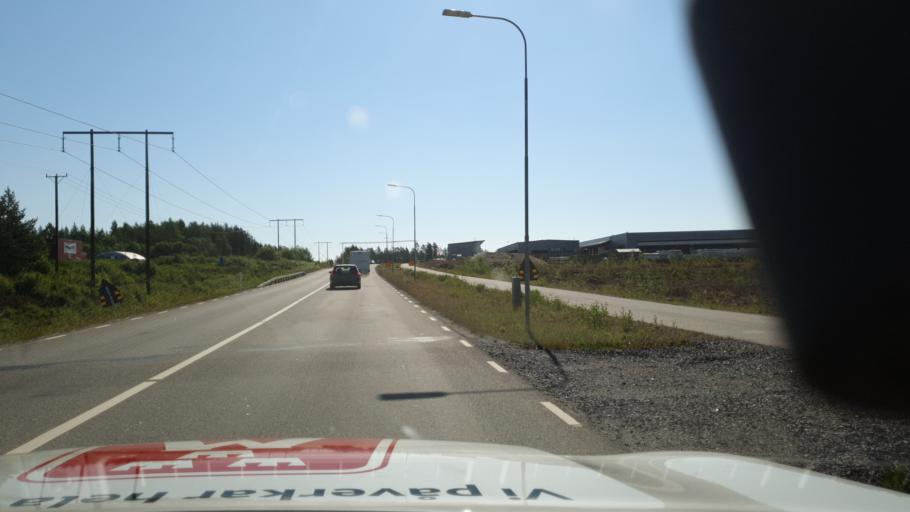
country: SE
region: Vaesterbotten
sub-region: Umea Kommun
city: Roback
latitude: 63.8491
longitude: 20.1491
